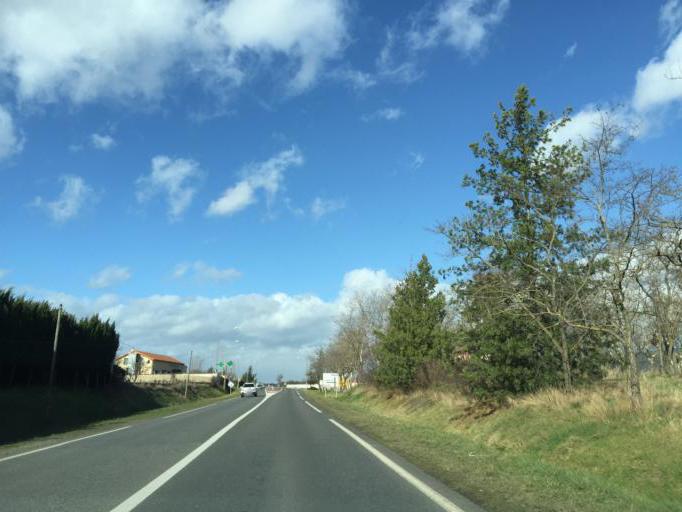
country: FR
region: Rhone-Alpes
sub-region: Departement de la Loire
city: Champdieu
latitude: 45.6441
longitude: 4.0514
